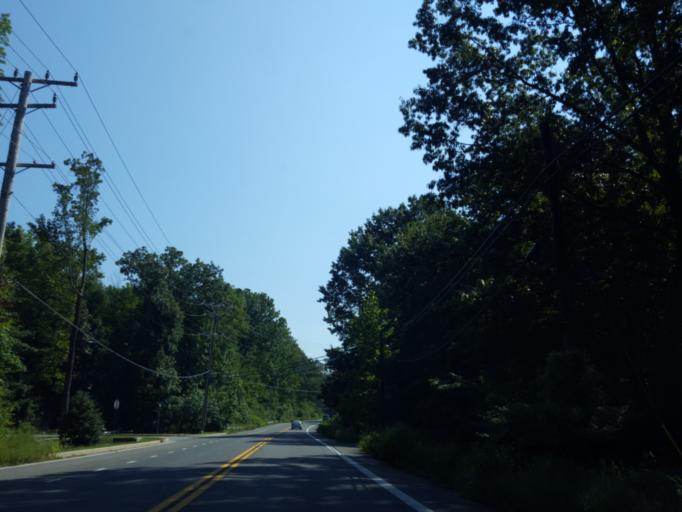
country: US
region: Maryland
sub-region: Anne Arundel County
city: Deale
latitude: 38.8147
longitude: -76.5497
